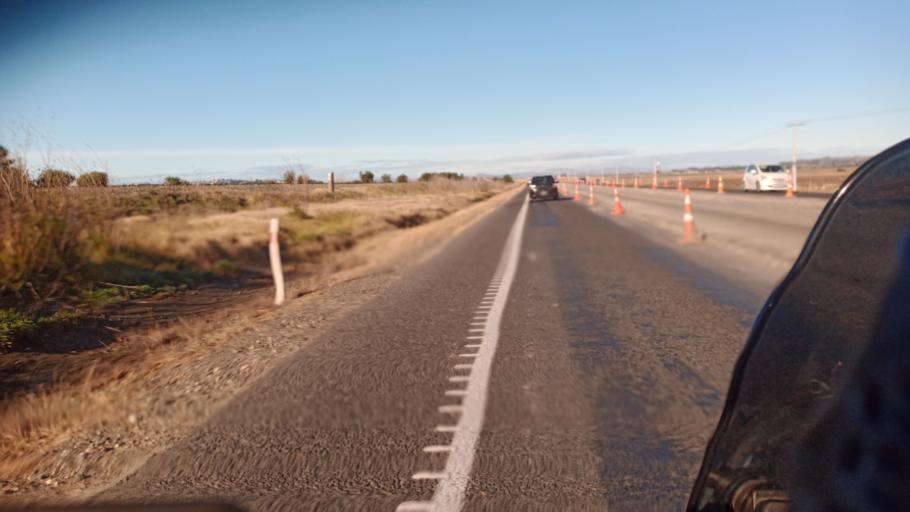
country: NZ
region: Hawke's Bay
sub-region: Napier City
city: Napier
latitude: -39.4437
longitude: 176.8712
